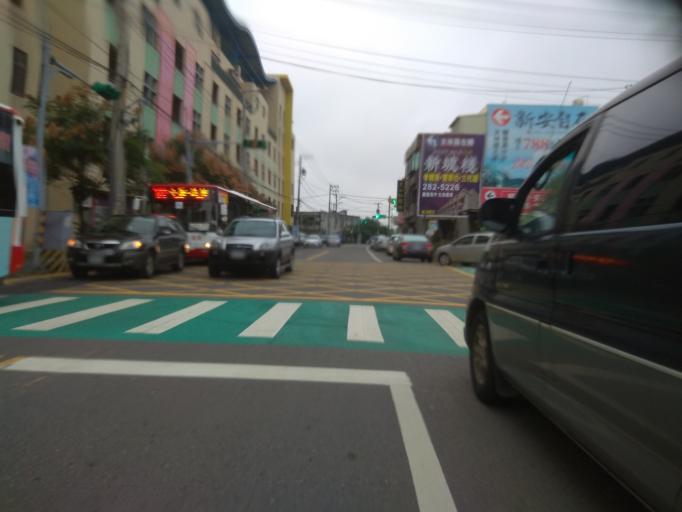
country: TW
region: Taiwan
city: Taoyuan City
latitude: 25.0147
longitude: 121.1338
